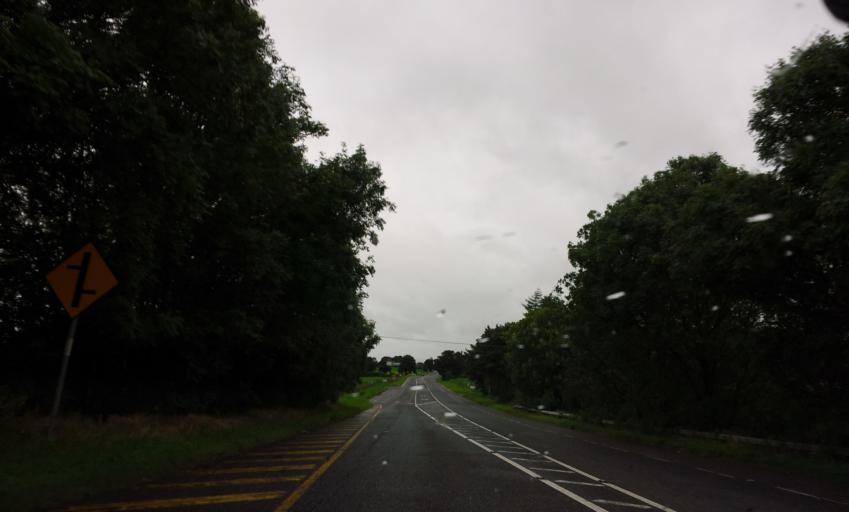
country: IE
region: Munster
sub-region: County Cork
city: Mitchelstown
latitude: 52.2797
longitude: -8.2477
